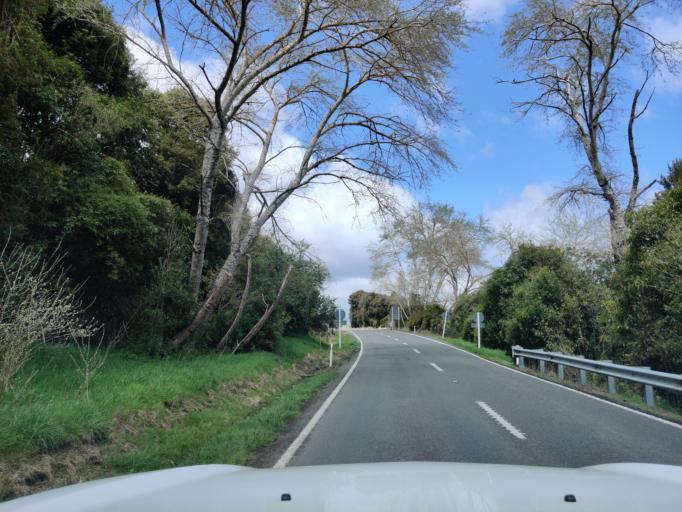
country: NZ
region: Manawatu-Wanganui
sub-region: Ruapehu District
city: Waiouru
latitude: -39.6482
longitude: 175.3243
